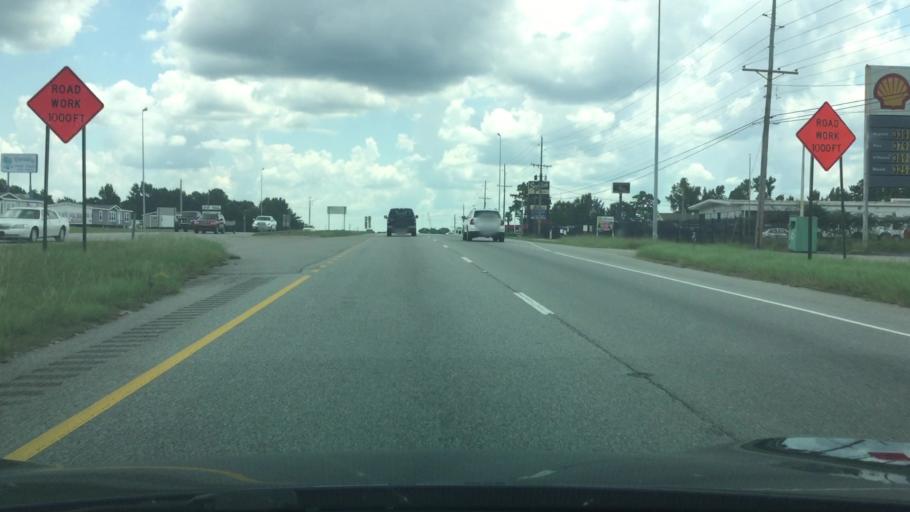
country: US
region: Alabama
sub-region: Pike County
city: Troy
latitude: 31.8049
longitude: -85.9875
